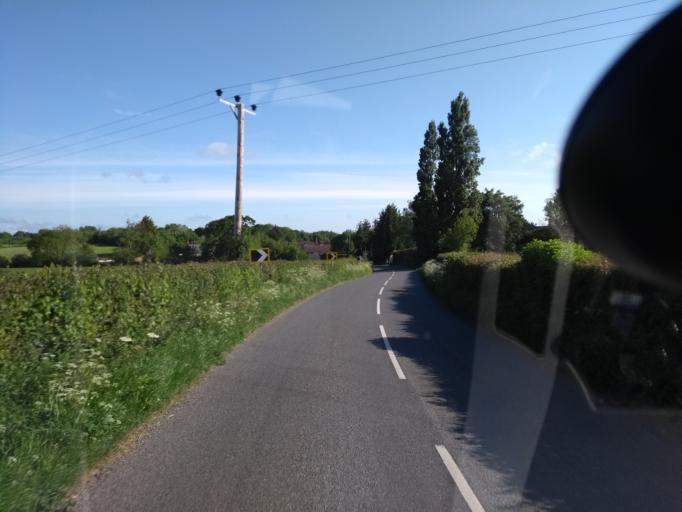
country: GB
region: England
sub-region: Somerset
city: Taunton
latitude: 50.9758
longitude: -3.1269
